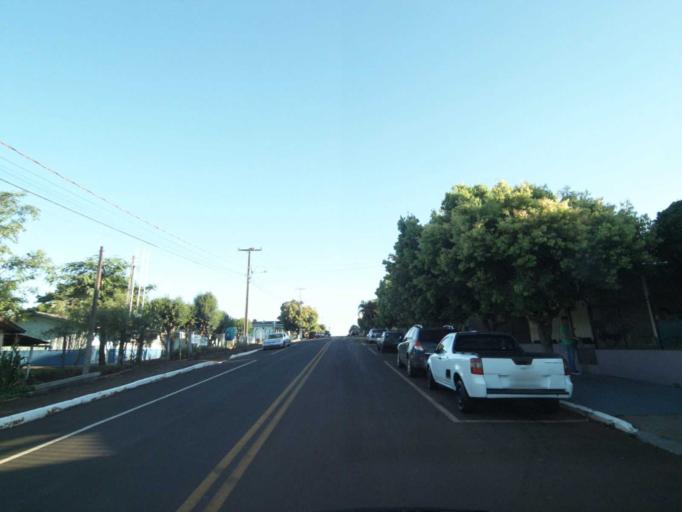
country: BR
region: Parana
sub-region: Coronel Vivida
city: Coronel Vivida
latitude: -25.9537
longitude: -52.8195
